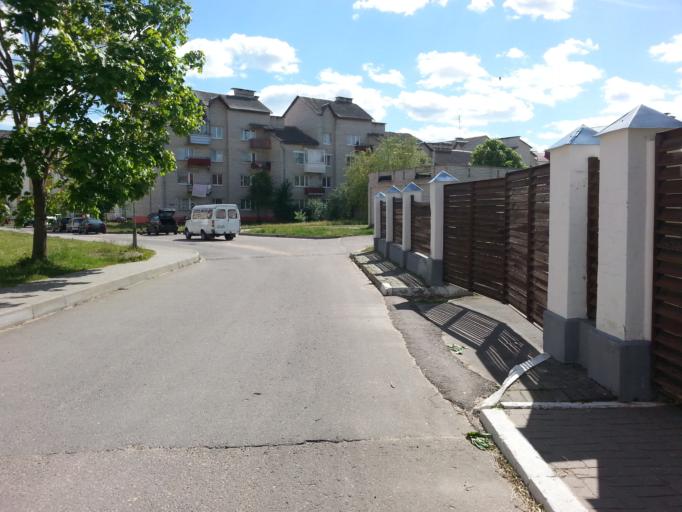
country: BY
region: Minsk
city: Narach
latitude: 54.9144
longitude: 26.7019
